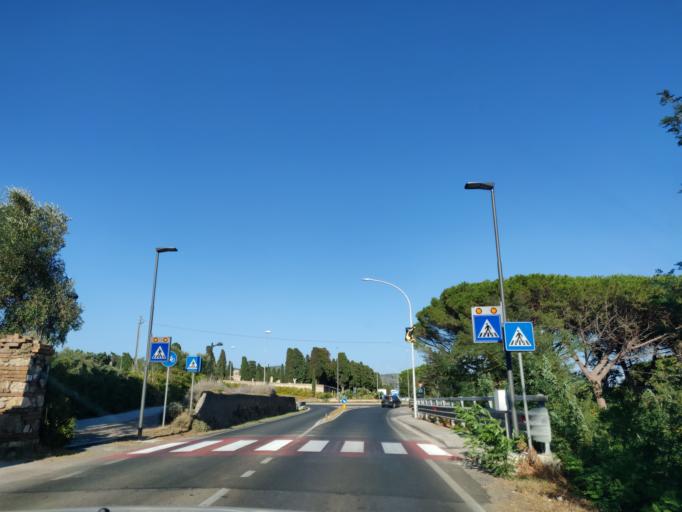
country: IT
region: Tuscany
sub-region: Provincia di Grosseto
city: Orbetello
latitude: 42.4443
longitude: 11.2313
